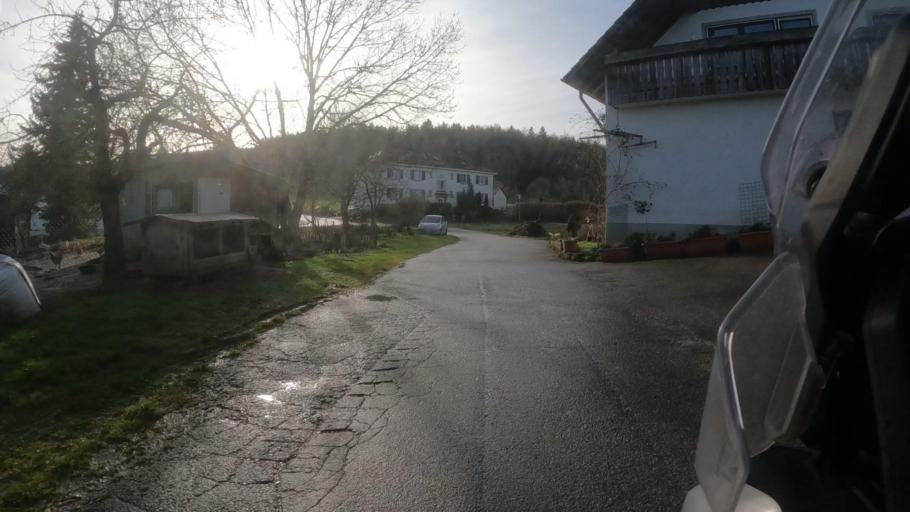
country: DE
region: Baden-Wuerttemberg
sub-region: Freiburg Region
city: Tengen
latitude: 47.7846
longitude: 8.6304
